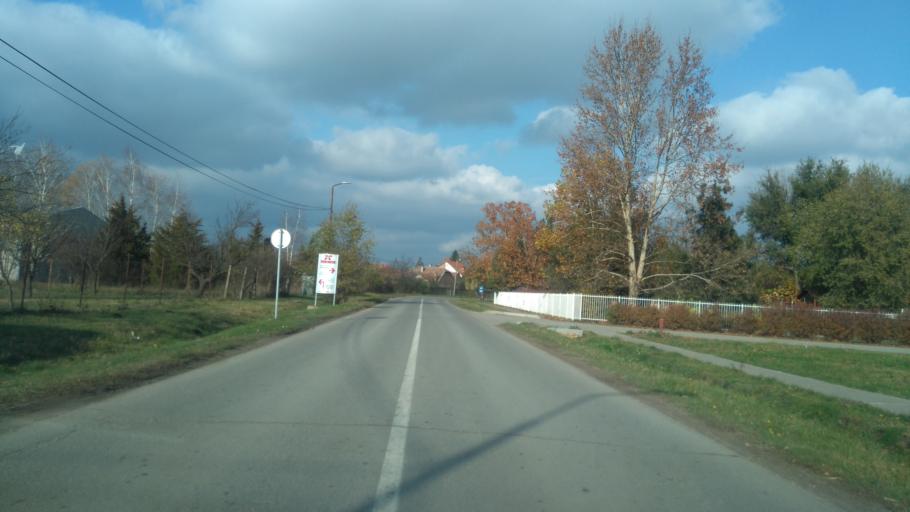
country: RS
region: Autonomna Pokrajina Vojvodina
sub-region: Severnobanatski Okrug
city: Ada
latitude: 45.7872
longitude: 20.1275
